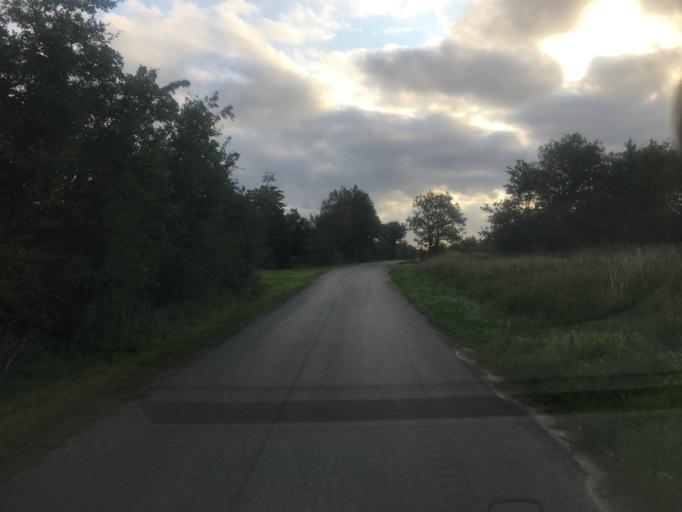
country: DK
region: South Denmark
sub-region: Tonder Kommune
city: Logumkloster
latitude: 55.0258
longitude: 8.9099
